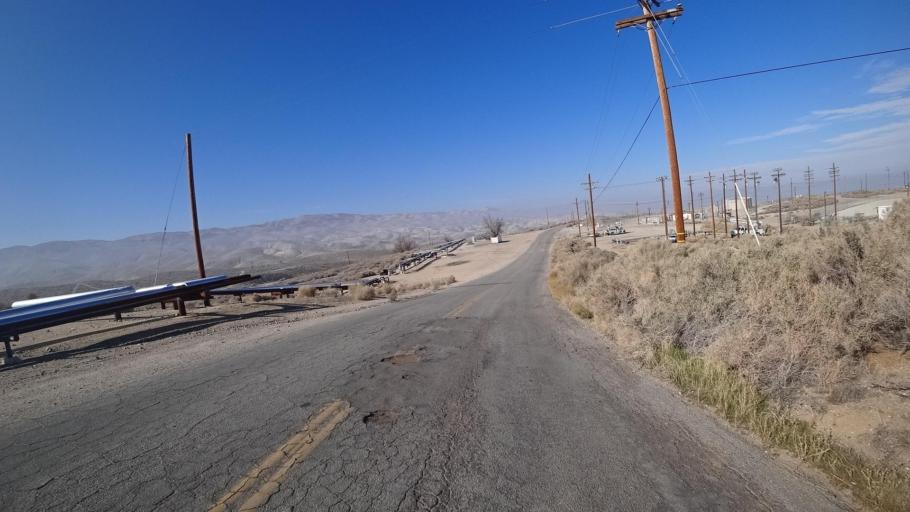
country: US
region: California
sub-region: Kern County
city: Taft Heights
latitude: 35.1138
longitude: -119.4737
